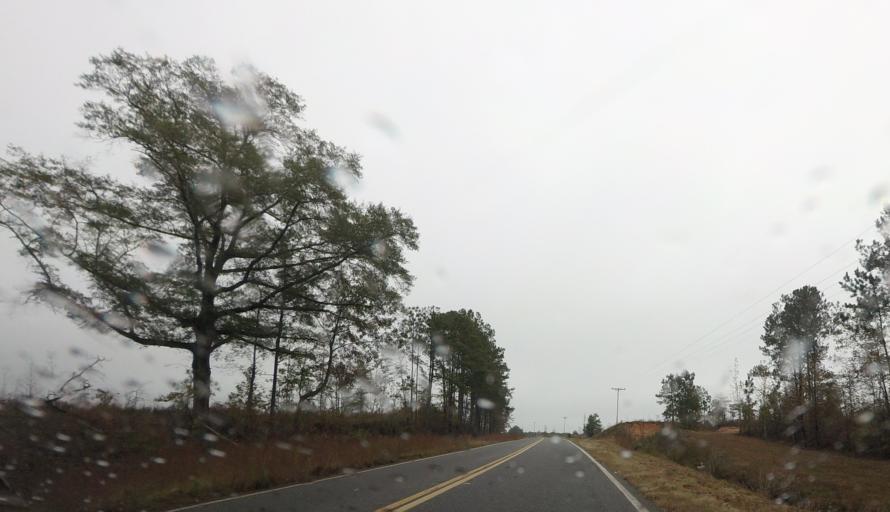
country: US
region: Georgia
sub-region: Taylor County
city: Butler
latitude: 32.4354
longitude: -84.3486
